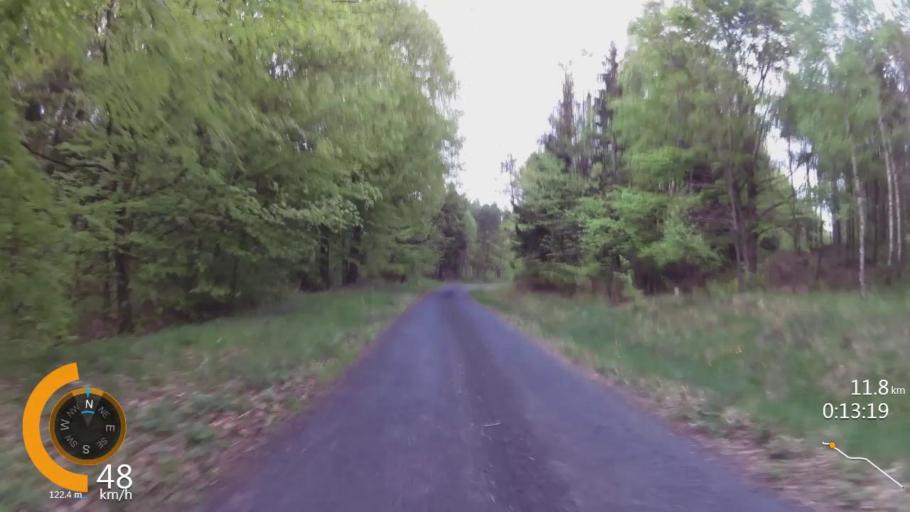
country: PL
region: West Pomeranian Voivodeship
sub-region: Powiat drawski
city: Wierzchowo
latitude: 53.5259
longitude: 16.0975
